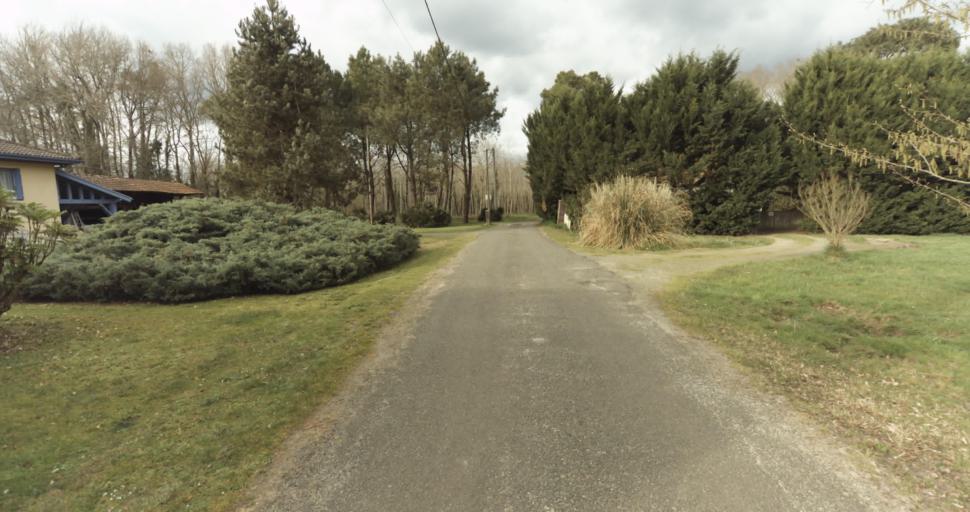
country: FR
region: Aquitaine
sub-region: Departement des Landes
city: Roquefort
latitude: 44.0415
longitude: -0.3248
